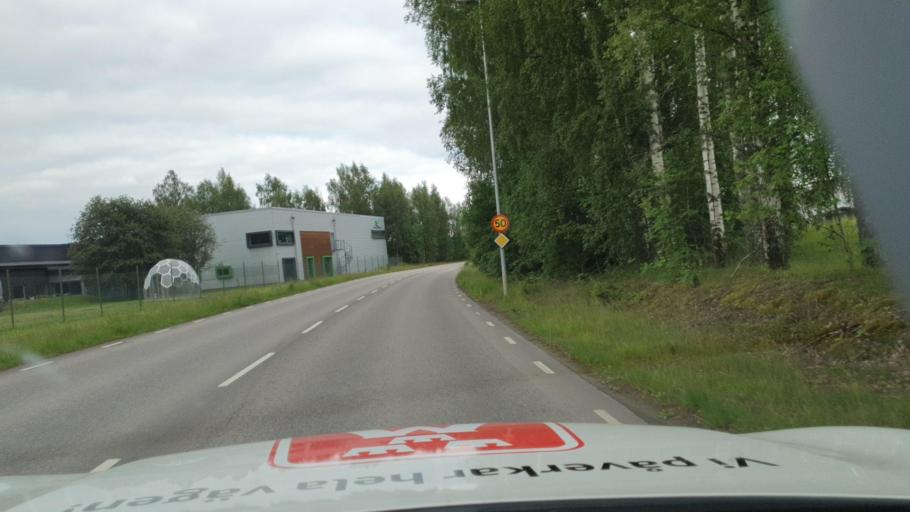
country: SE
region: Vaermland
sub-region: Forshaga Kommun
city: Forshaga
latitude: 59.4476
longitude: 13.4362
